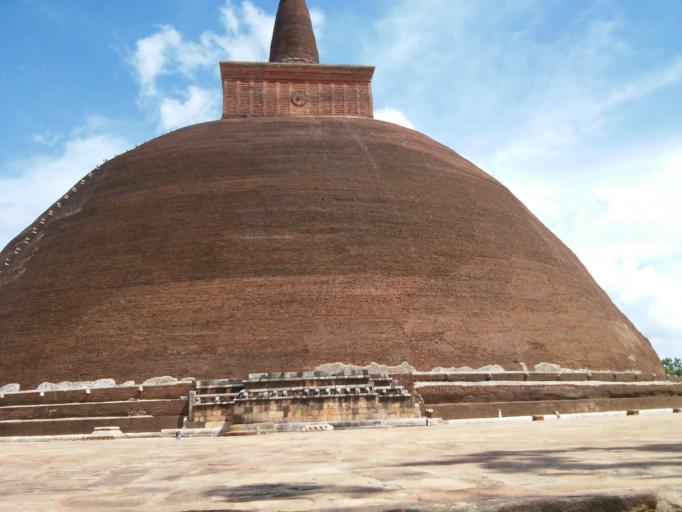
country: LK
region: North Central
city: Anuradhapura
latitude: 8.3718
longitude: 80.3952
